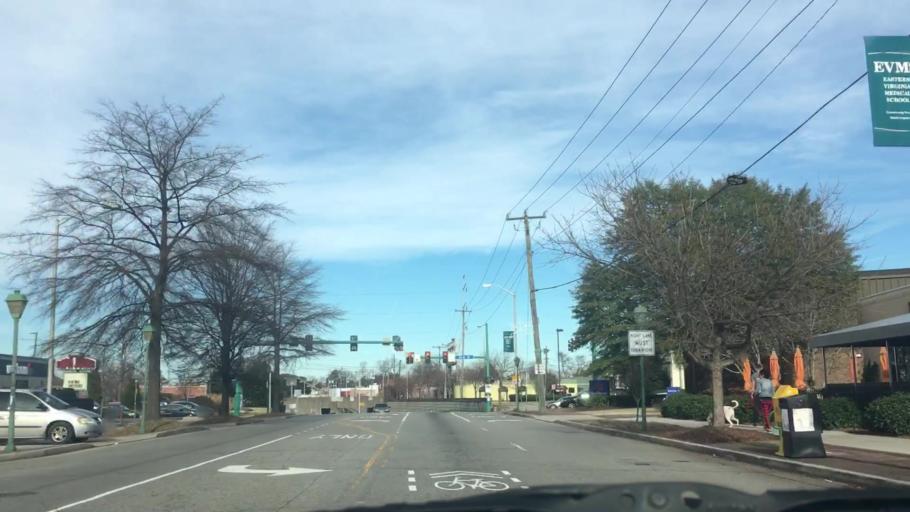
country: US
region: Virginia
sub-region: City of Norfolk
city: Norfolk
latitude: 36.8703
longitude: -76.2966
